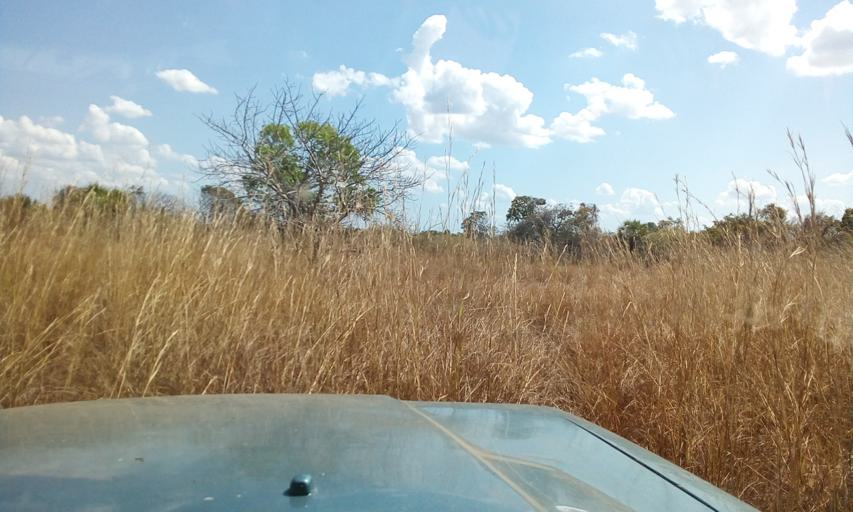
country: MG
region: Melaky
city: Mahabe
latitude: -16.4377
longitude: 45.3778
